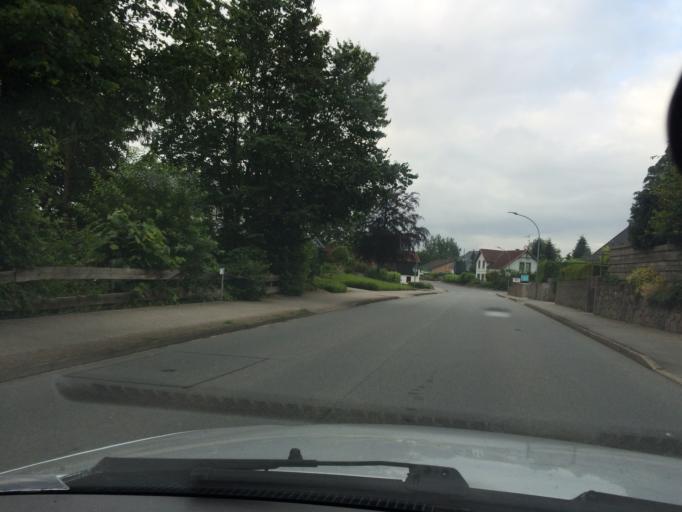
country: DE
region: Schleswig-Holstein
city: Oeversee
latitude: 54.6943
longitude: 9.4269
